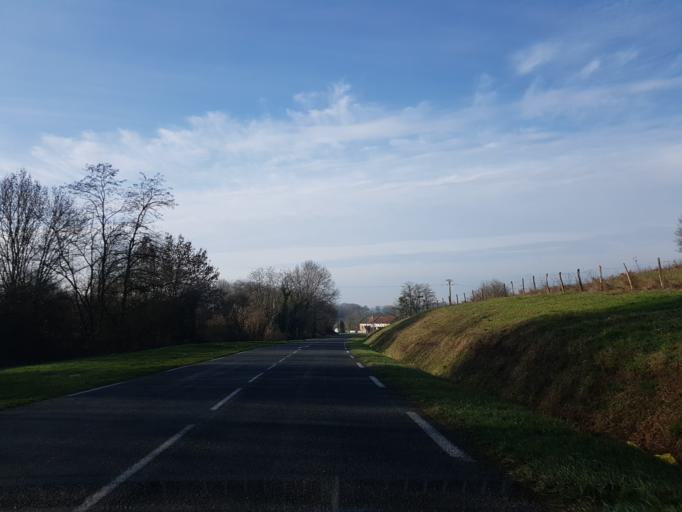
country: FR
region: Bourgogne
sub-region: Departement de Saone-et-Loire
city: La Motte-Saint-Jean
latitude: 46.5960
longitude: 3.9484
